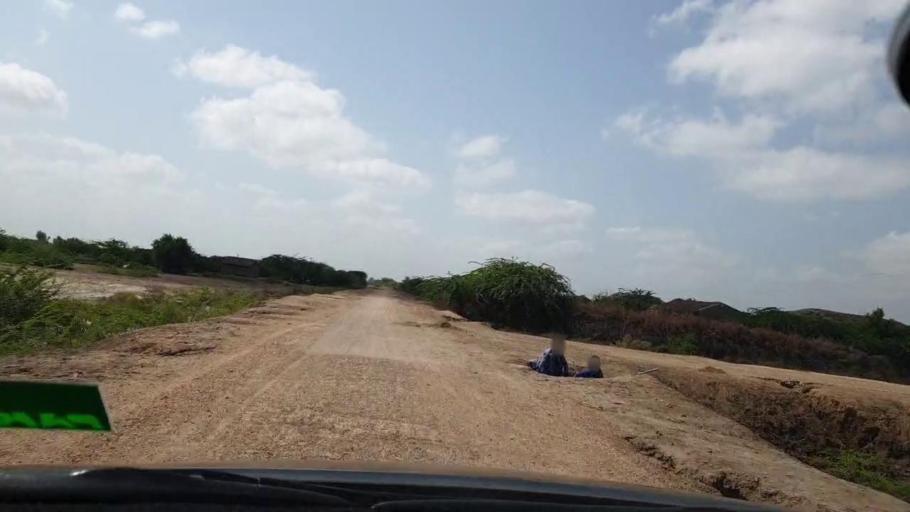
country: PK
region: Sindh
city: Kadhan
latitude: 24.5810
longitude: 69.1521
